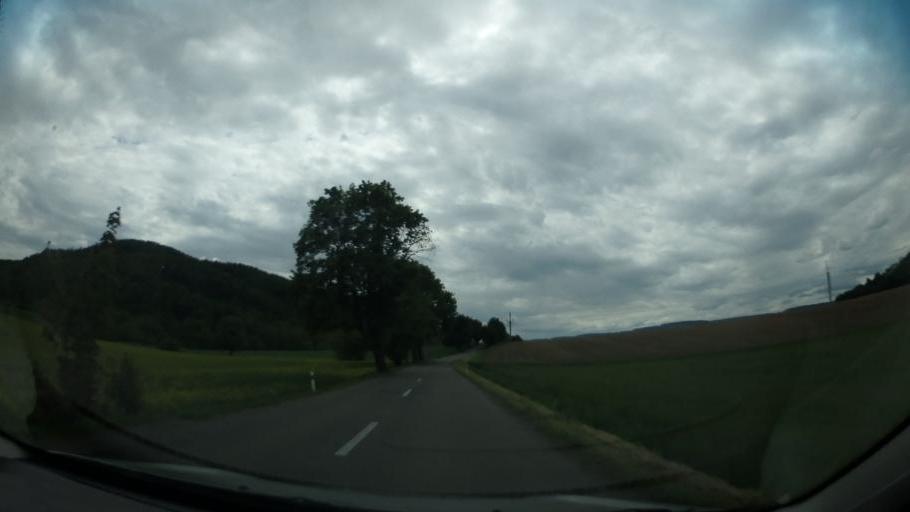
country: CZ
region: Pardubicky
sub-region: Okres Svitavy
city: Moravska Trebova
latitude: 49.7886
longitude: 16.6713
